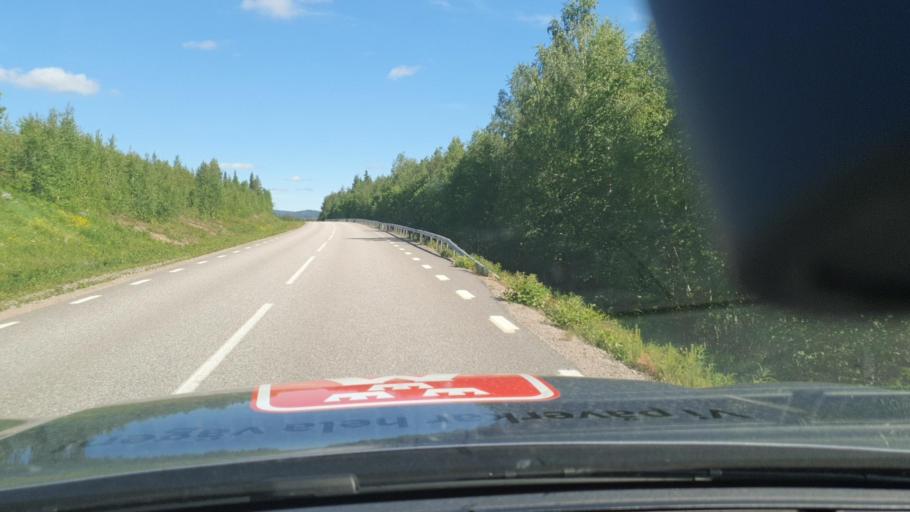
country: SE
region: Norrbotten
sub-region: Overkalix Kommun
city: OEverkalix
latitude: 66.7490
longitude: 22.6715
